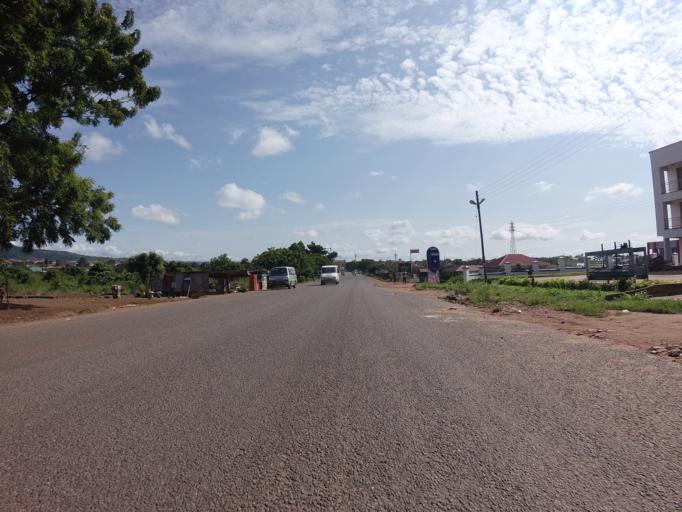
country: GH
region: Eastern
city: Aburi
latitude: 5.7844
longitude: -0.1327
